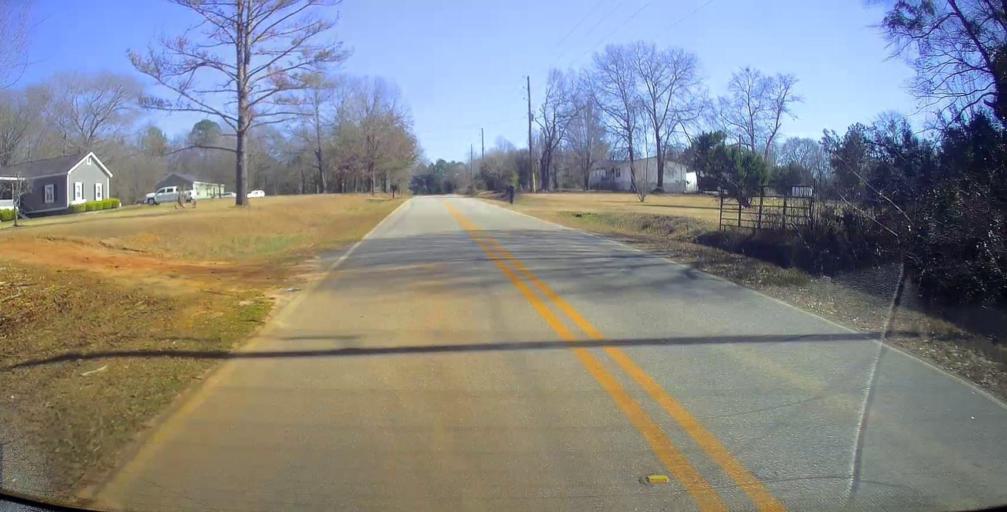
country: US
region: Georgia
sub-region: Peach County
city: Byron
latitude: 32.6205
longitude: -83.7831
